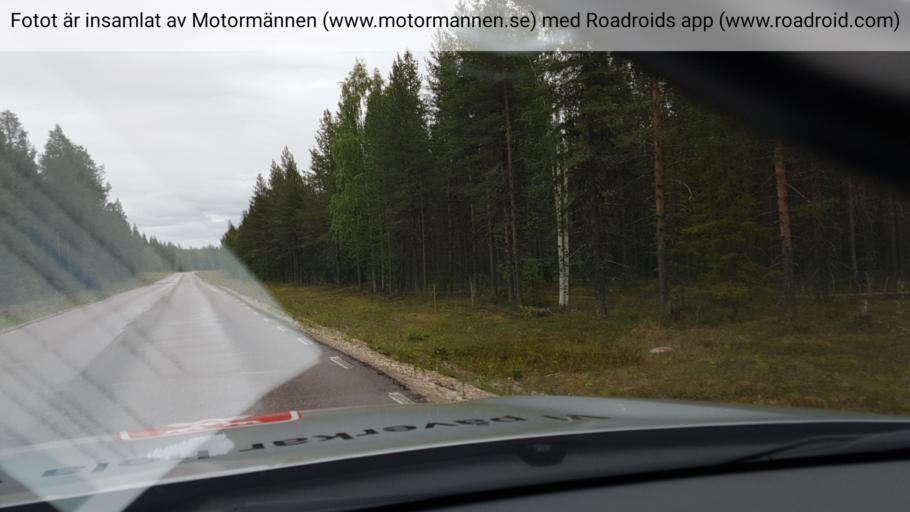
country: SE
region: Norrbotten
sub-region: Overkalix Kommun
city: OEverkalix
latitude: 67.0620
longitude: 22.2815
